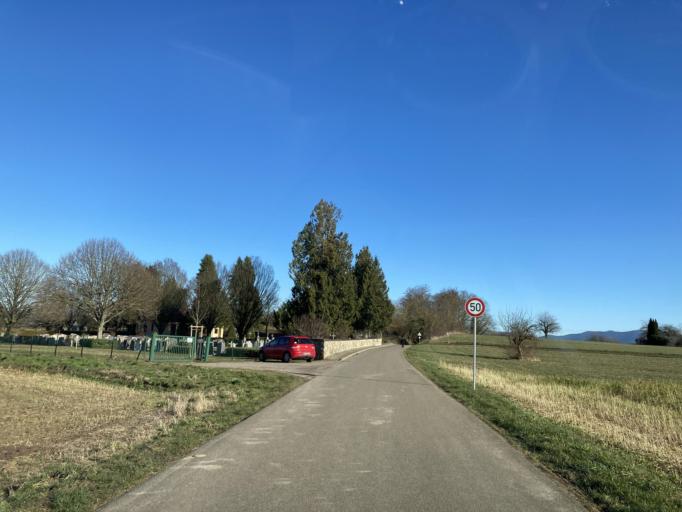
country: DE
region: Baden-Wuerttemberg
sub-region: Freiburg Region
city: Umkirch
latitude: 48.0705
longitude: 7.7897
